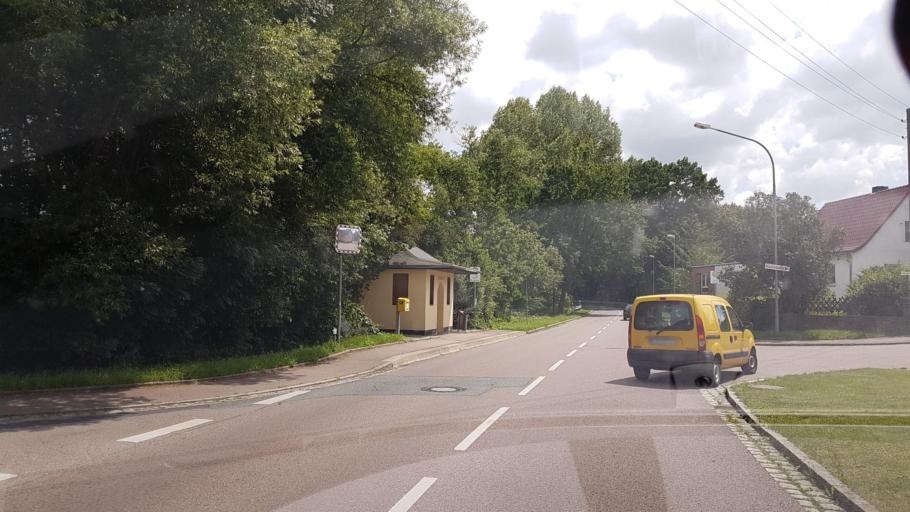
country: DE
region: Saxony
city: Nunchritz
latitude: 51.2830
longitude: 13.4079
